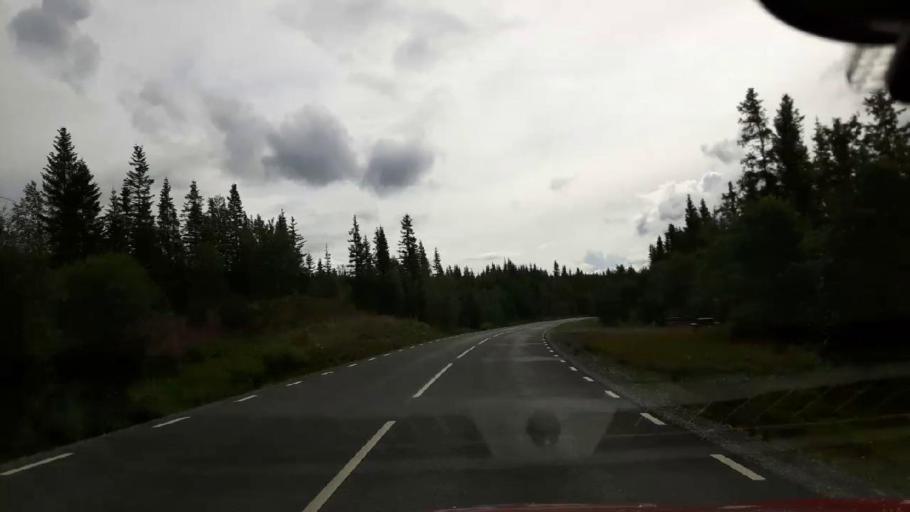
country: NO
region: Nord-Trondelag
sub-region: Lierne
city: Sandvika
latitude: 64.6453
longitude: 14.1422
